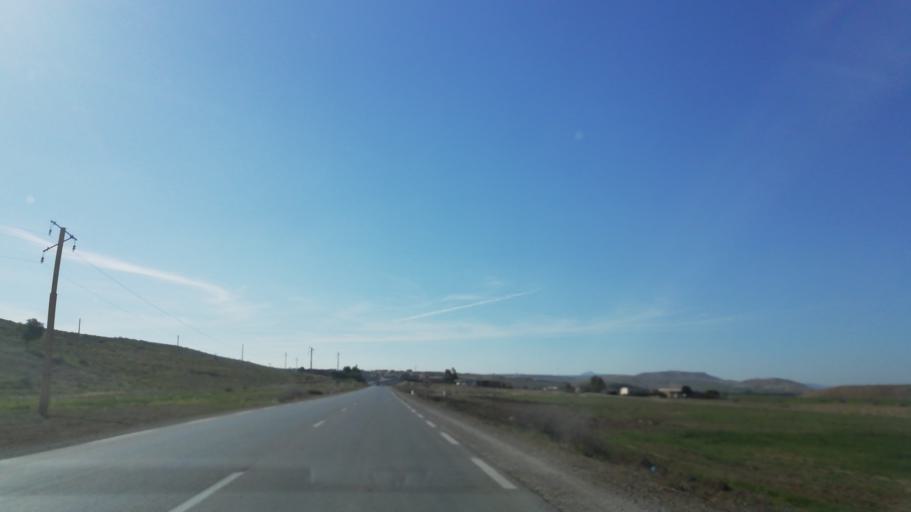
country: DZ
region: Mascara
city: Oued el Abtal
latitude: 35.4555
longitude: 0.7298
